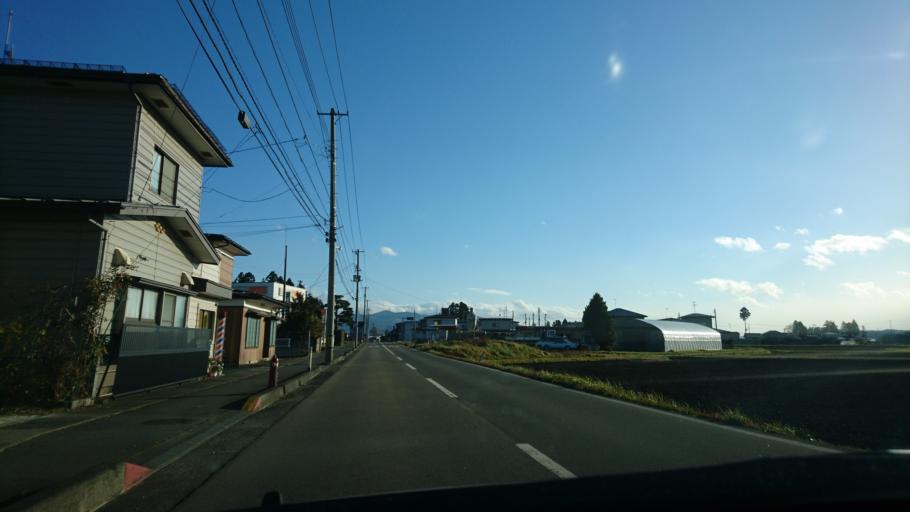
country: JP
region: Iwate
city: Mizusawa
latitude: 39.1122
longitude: 141.1552
